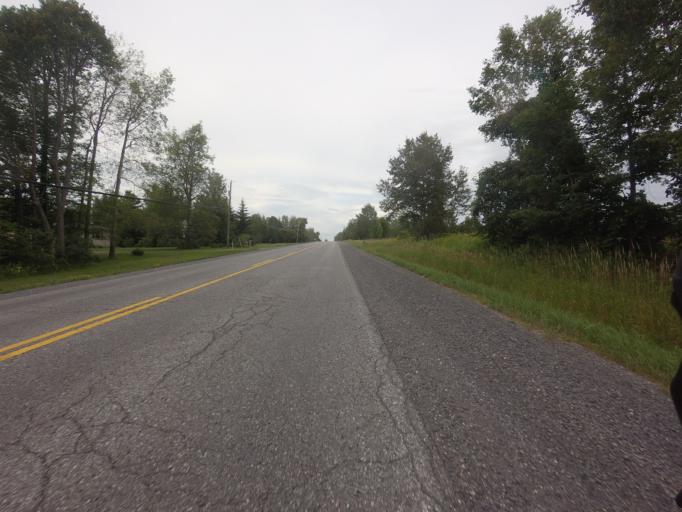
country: CA
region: Ontario
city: Carleton Place
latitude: 45.1518
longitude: -76.3079
